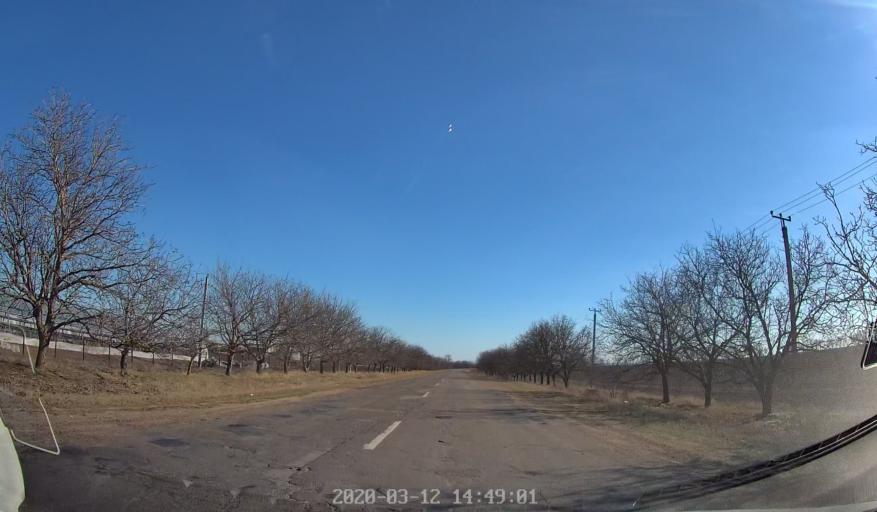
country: MD
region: Criuleni
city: Criuleni
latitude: 47.2274
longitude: 29.1429
